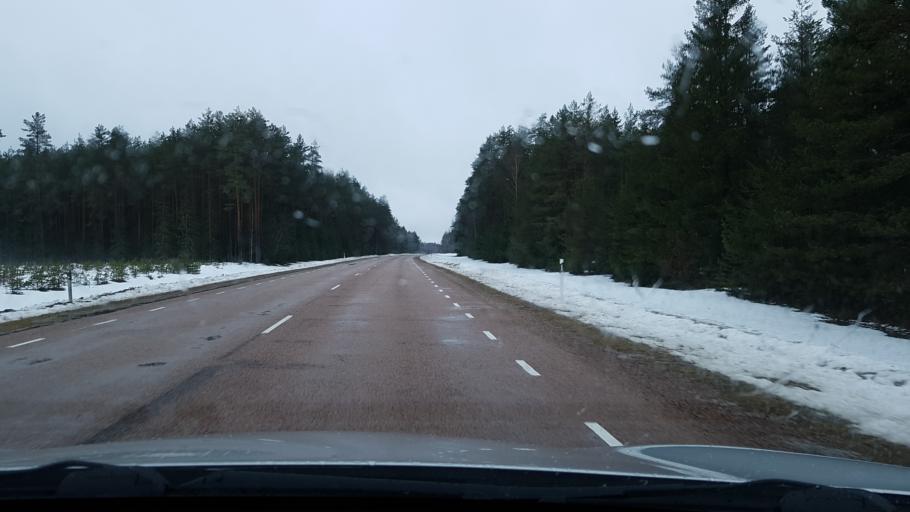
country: EE
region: Vorumaa
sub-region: Voru linn
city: Voru
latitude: 57.7621
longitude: 26.8468
